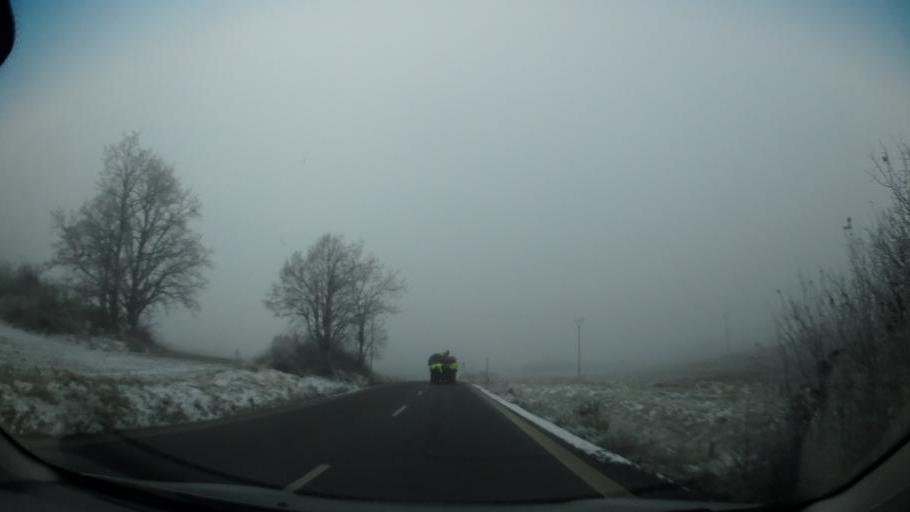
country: CZ
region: Vysocina
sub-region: Okres Trebic
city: Trebic
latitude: 49.2453
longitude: 15.9014
